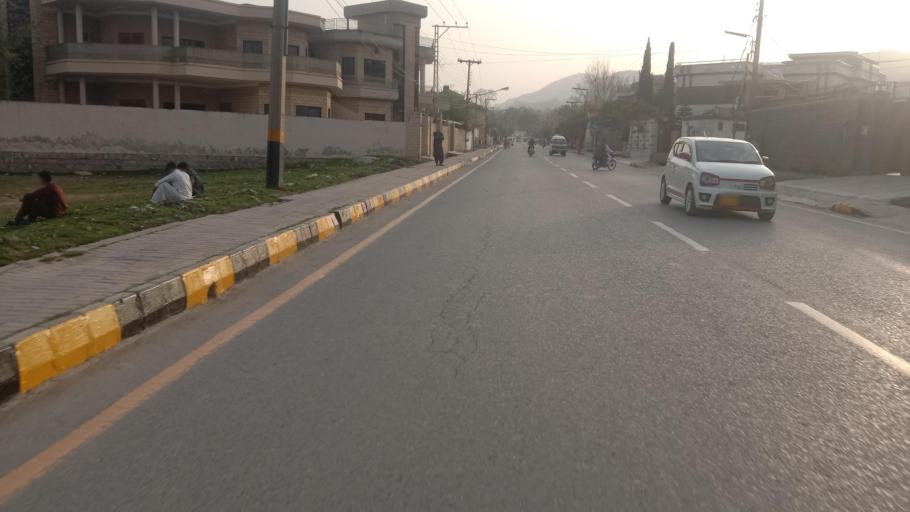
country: PK
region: Khyber Pakhtunkhwa
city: Abbottabad
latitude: 34.1688
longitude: 73.2301
